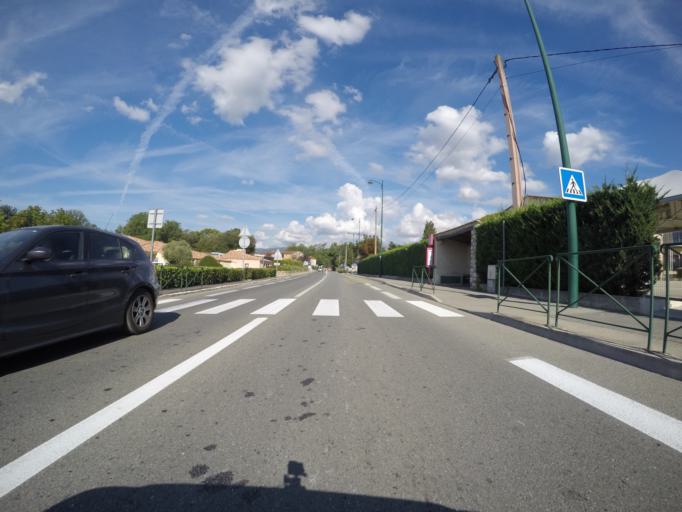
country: FR
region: Provence-Alpes-Cote d'Azur
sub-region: Departement des Alpes-Maritimes
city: Le Rouret
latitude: 43.6662
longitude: 7.0509
